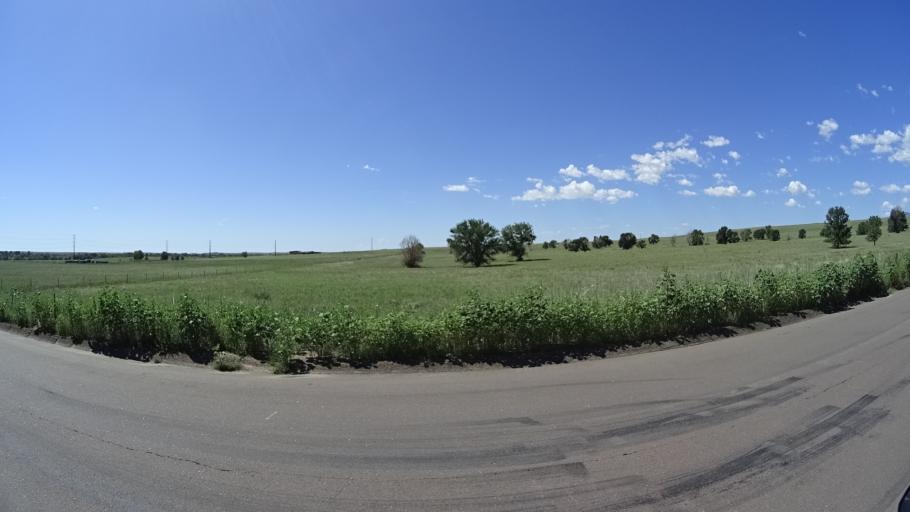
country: US
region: Colorado
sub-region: El Paso County
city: Security-Widefield
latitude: 38.7810
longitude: -104.6692
